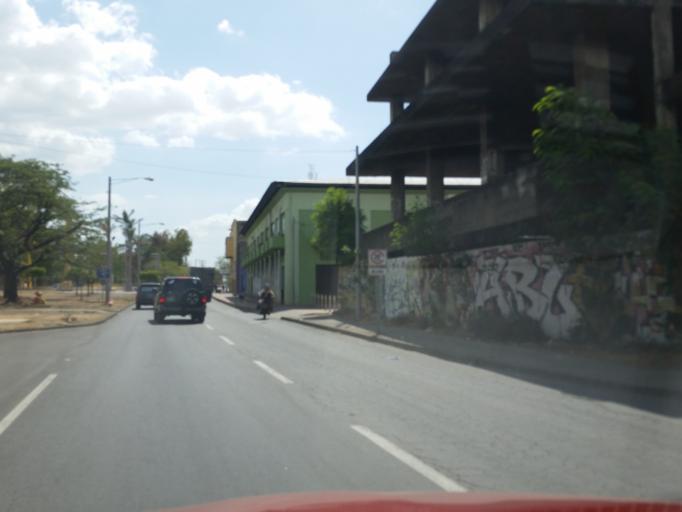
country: NI
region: Managua
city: Managua
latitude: 12.1547
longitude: -86.2722
